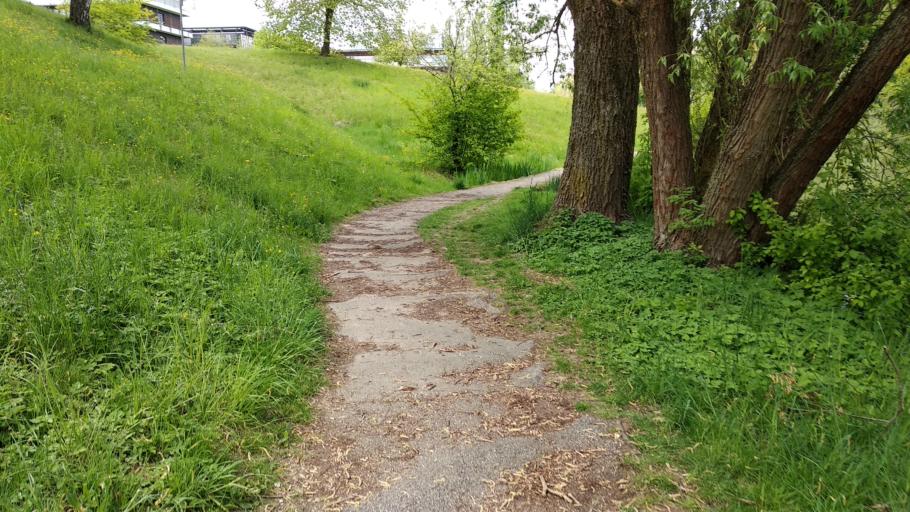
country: DE
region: Bavaria
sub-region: Upper Bavaria
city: Freising
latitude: 48.4003
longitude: 11.7233
